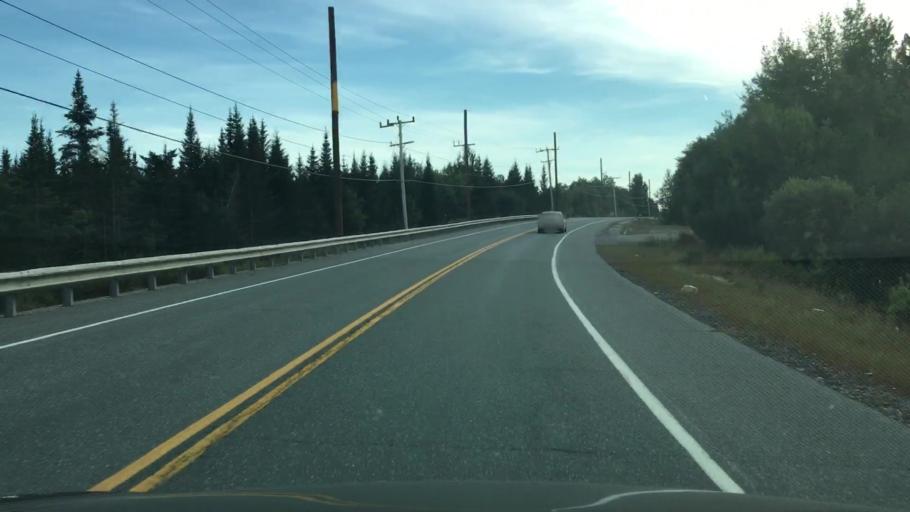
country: US
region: Maine
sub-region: Hancock County
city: Surry
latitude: 44.4610
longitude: -68.5383
